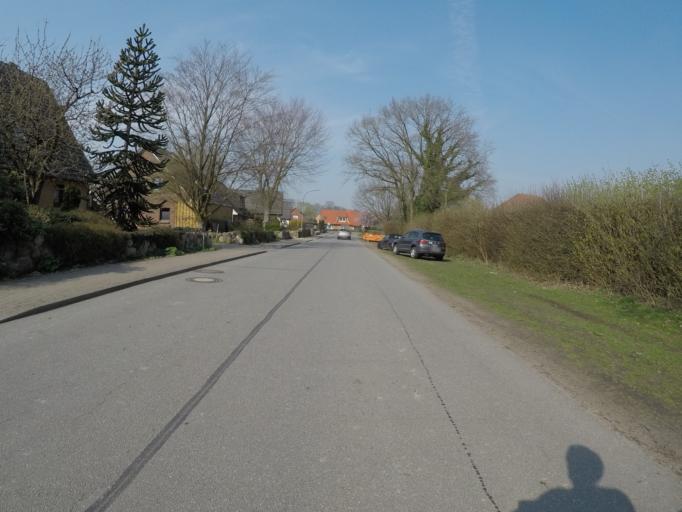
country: DE
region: Schleswig-Holstein
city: Gross Niendorf
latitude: 53.8441
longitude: 10.2404
